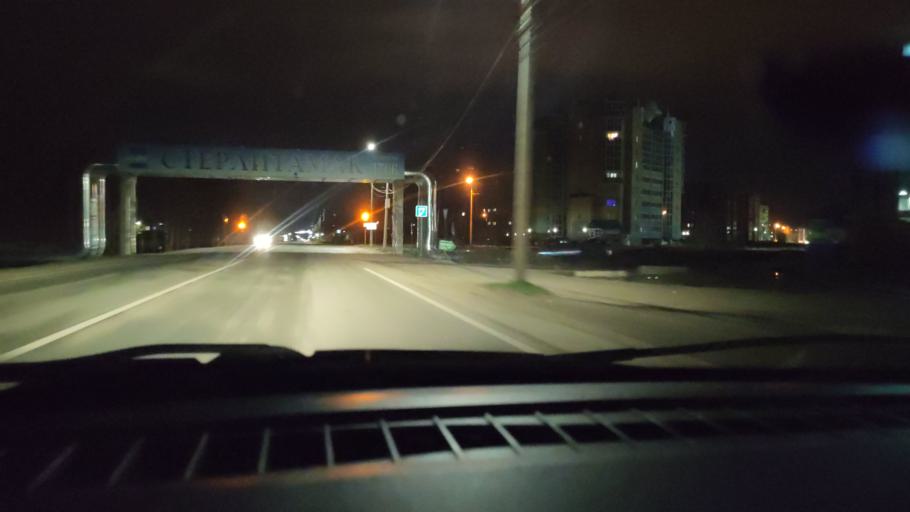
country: RU
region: Bashkortostan
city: Sterlitamak
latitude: 53.6418
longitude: 55.8980
